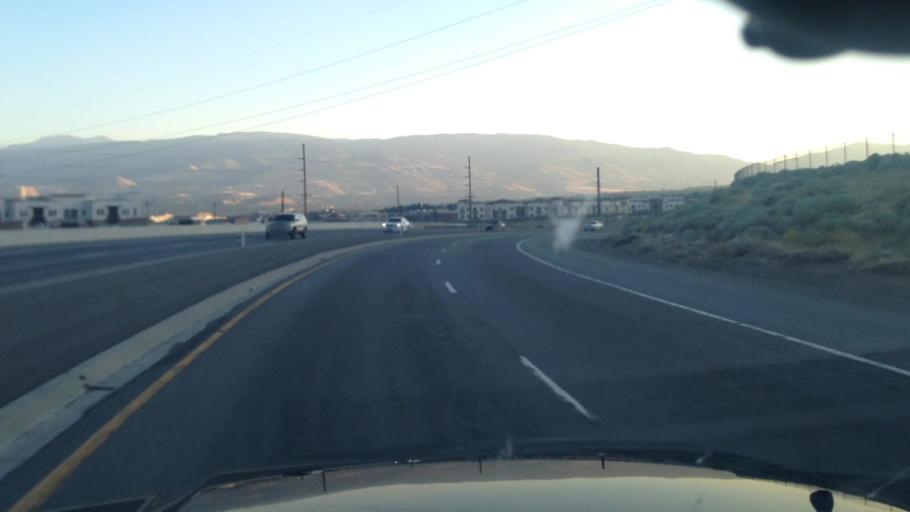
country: US
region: Nevada
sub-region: Washoe County
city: Reno
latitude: 39.5536
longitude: -119.8051
